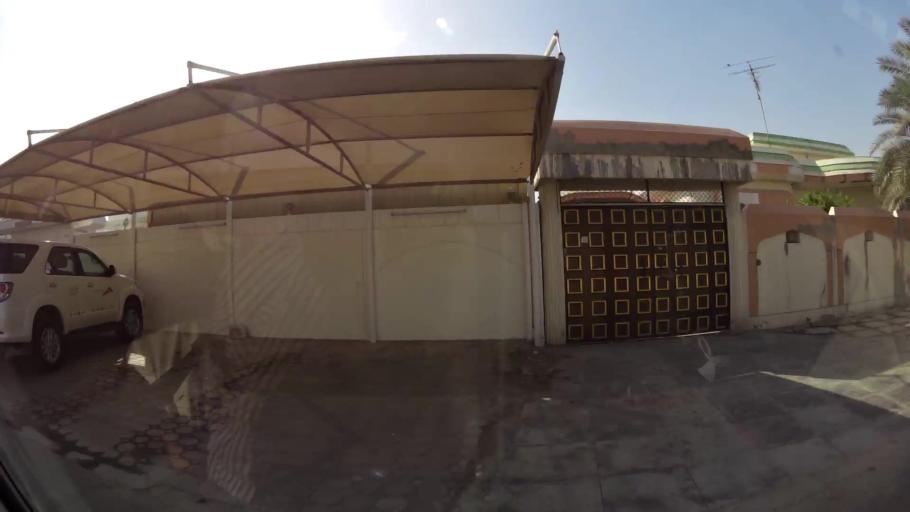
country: AE
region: Ash Shariqah
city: Sharjah
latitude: 25.2600
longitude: 55.3971
